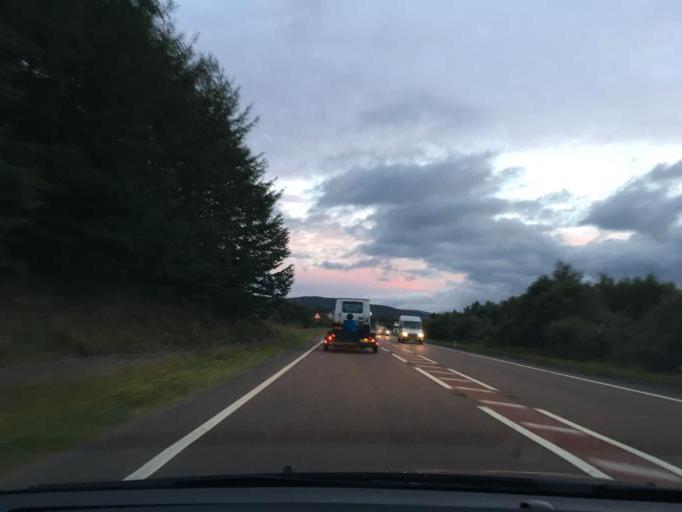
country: GB
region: Scotland
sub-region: Highland
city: Kingussie
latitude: 57.0308
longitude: -4.1566
